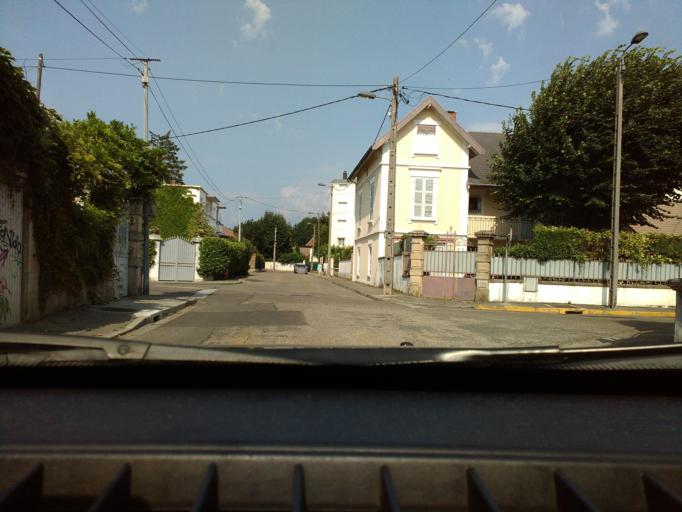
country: FR
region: Rhone-Alpes
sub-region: Departement de l'Isere
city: Grenoble
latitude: 45.1775
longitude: 5.7376
